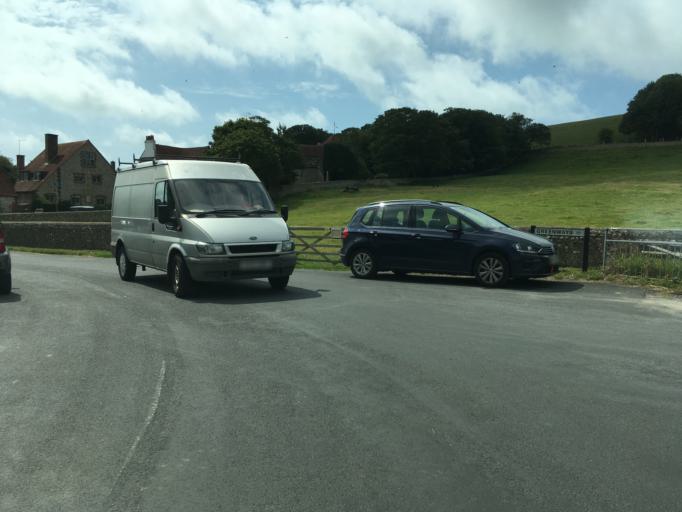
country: GB
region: England
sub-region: Brighton and Hove
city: Rottingdean
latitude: 50.8168
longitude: -0.0771
